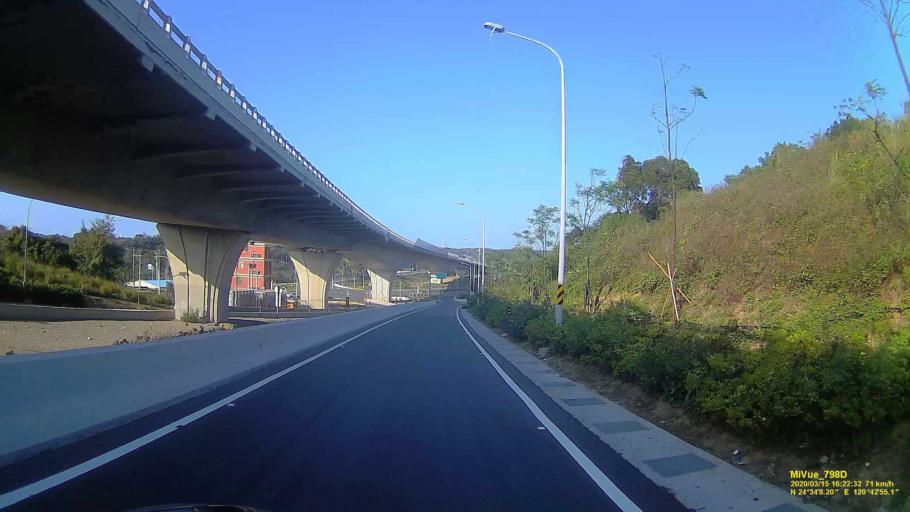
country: TW
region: Taiwan
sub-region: Miaoli
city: Miaoli
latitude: 24.5693
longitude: 120.7155
